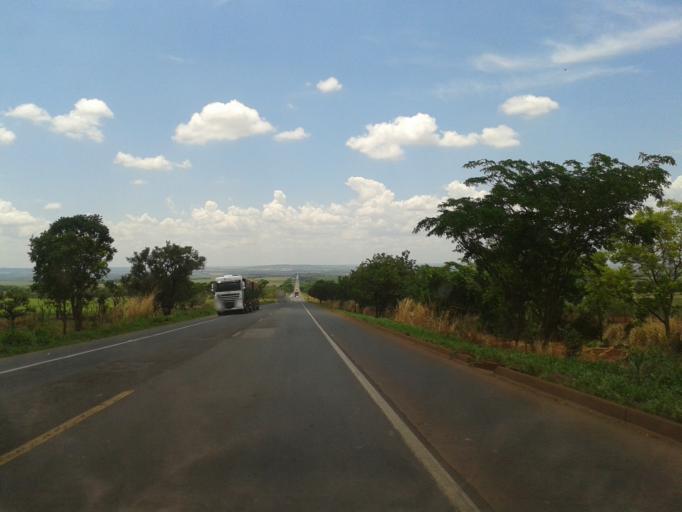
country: BR
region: Goias
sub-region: Goiatuba
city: Goiatuba
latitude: -18.2601
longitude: -49.6674
